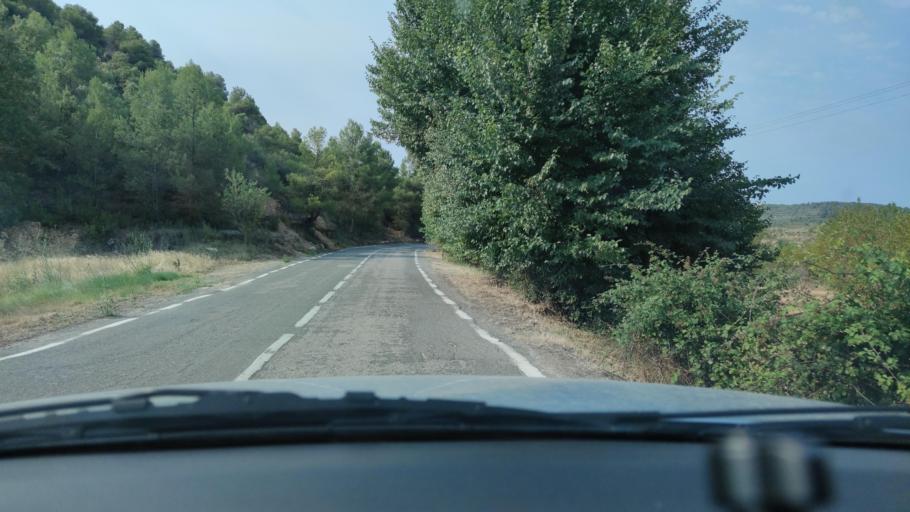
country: ES
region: Catalonia
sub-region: Provincia de Lleida
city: Juncosa
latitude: 41.4326
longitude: 0.8622
